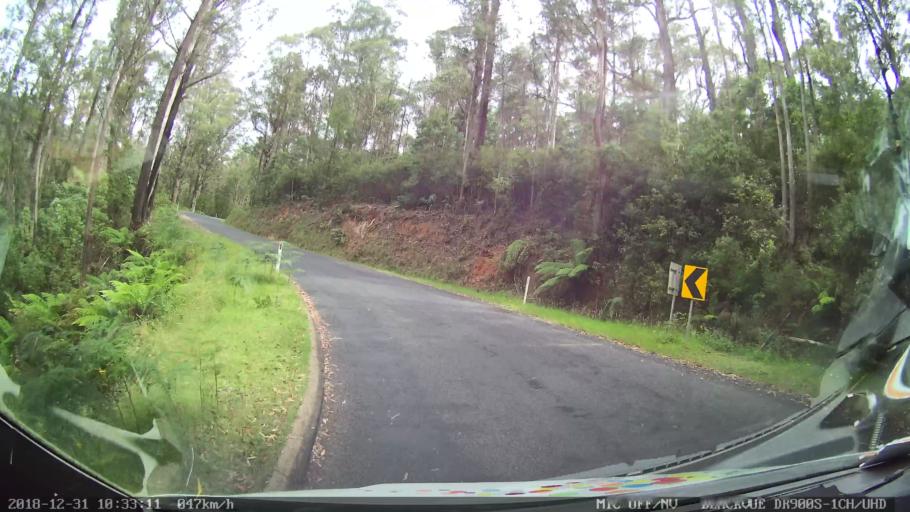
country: AU
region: New South Wales
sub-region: Snowy River
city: Jindabyne
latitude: -36.4482
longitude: 148.1645
